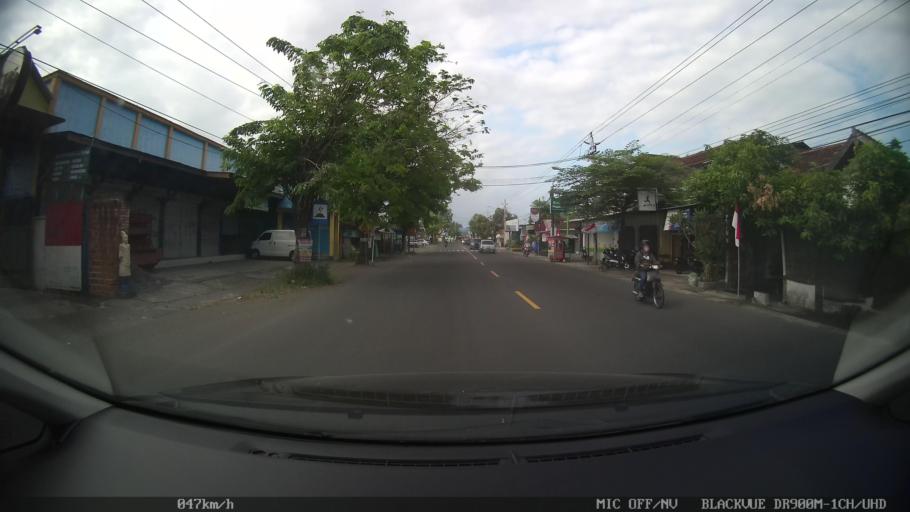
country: ID
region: Daerah Istimewa Yogyakarta
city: Kasihan
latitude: -7.8363
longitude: 110.3522
